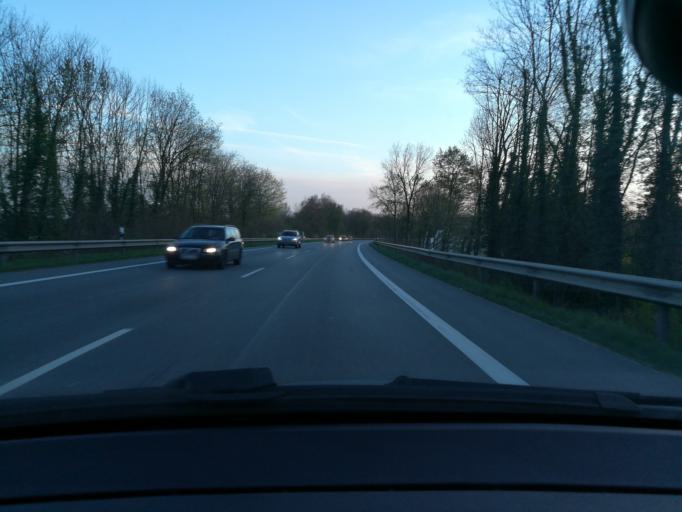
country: DE
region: North Rhine-Westphalia
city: Halle
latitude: 52.0596
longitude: 8.3469
